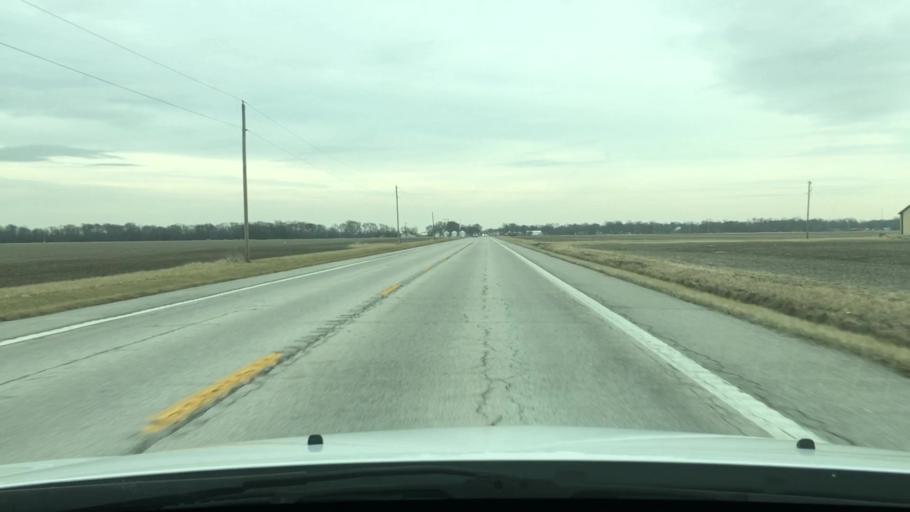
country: US
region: Missouri
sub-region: Audrain County
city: Vandalia
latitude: 39.2798
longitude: -91.5971
